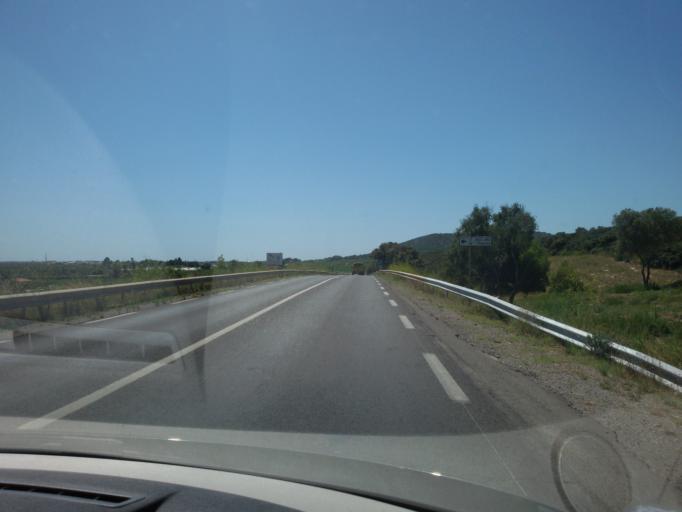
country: FR
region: Languedoc-Roussillon
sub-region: Departement de l'Herault
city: Vic-la-Gardiole
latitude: 43.4949
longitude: 3.7764
